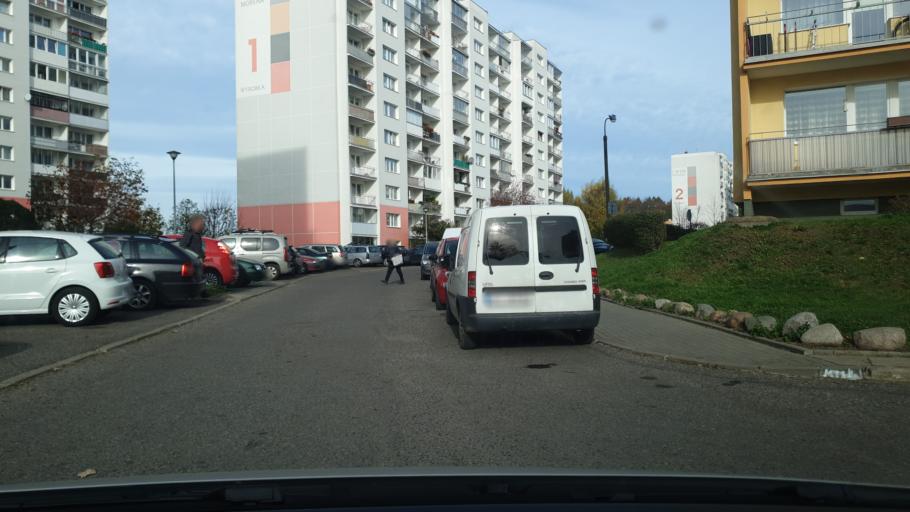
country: PL
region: Pomeranian Voivodeship
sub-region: Powiat gdanski
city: Kowale
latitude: 54.3589
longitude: 18.5764
